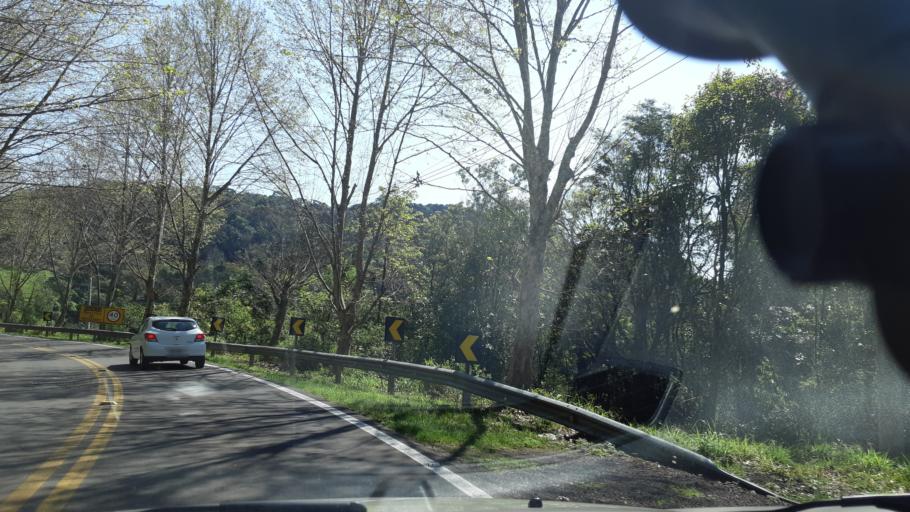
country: BR
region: Rio Grande do Sul
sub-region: Nova Petropolis
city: Nova Petropolis
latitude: -29.3935
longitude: -51.1231
